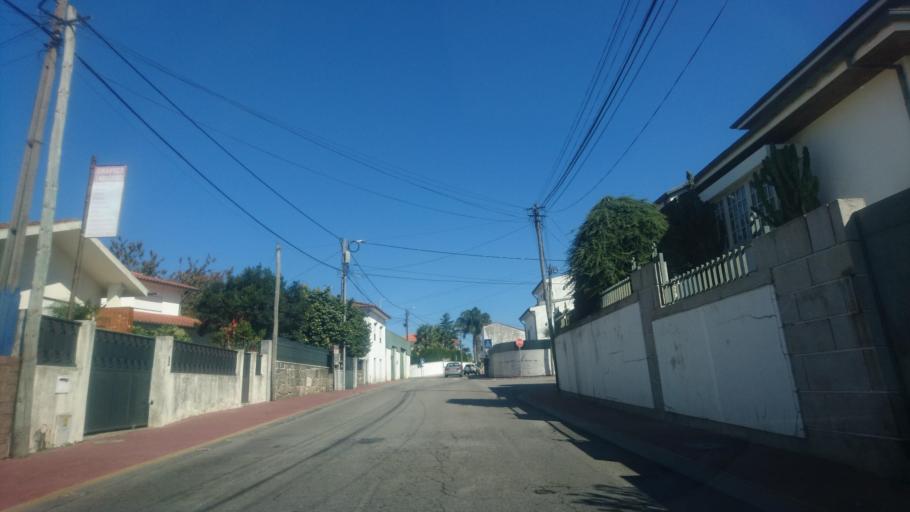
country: PT
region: Aveiro
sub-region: Santa Maria da Feira
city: Lamas
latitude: 40.9820
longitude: -8.5752
